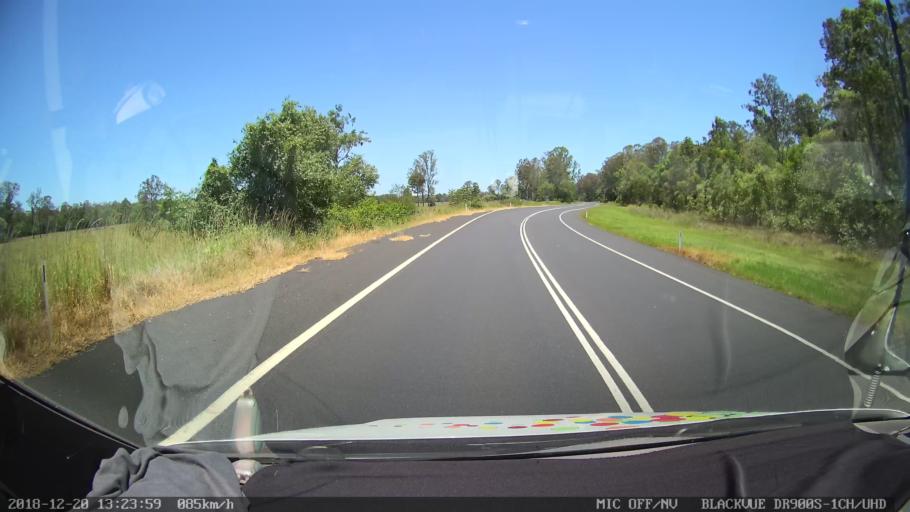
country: AU
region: New South Wales
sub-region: Richmond Valley
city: Casino
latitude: -29.1115
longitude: 153.0005
